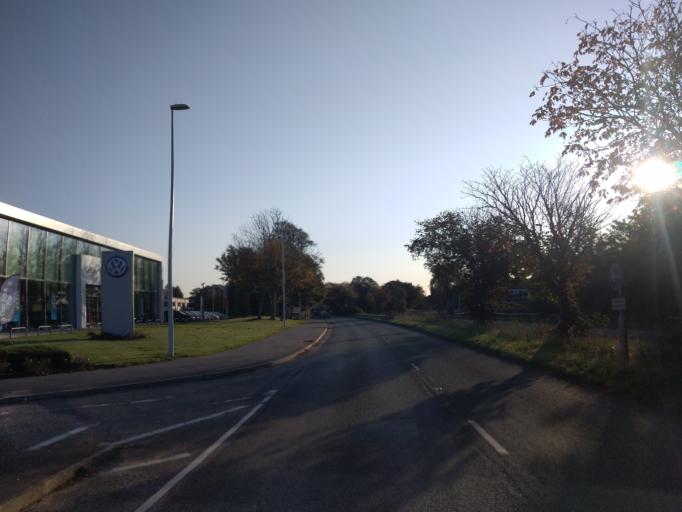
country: GB
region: England
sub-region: West Sussex
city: Goring-by-Sea
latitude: 50.8225
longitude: -0.4309
